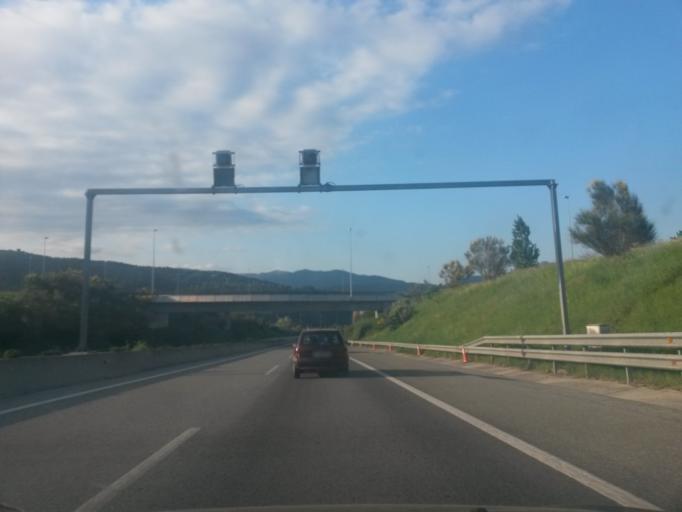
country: ES
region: Catalonia
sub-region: Provincia de Girona
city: Sant Joan les Fonts
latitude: 42.2089
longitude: 2.5388
